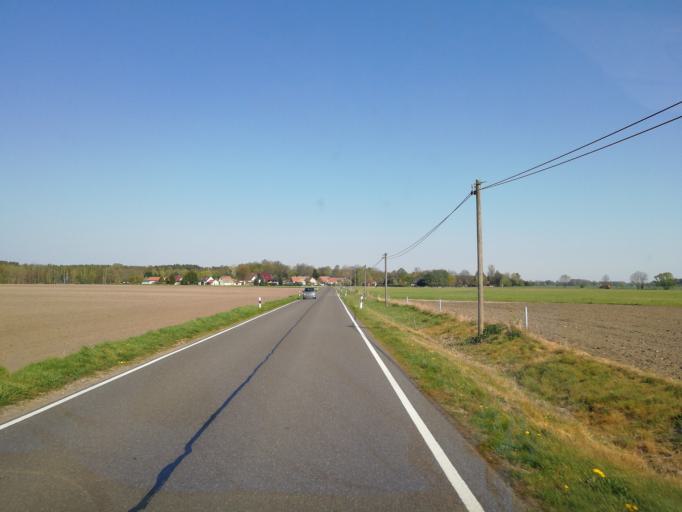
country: DE
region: Brandenburg
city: Crinitz
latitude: 51.7331
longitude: 13.8526
